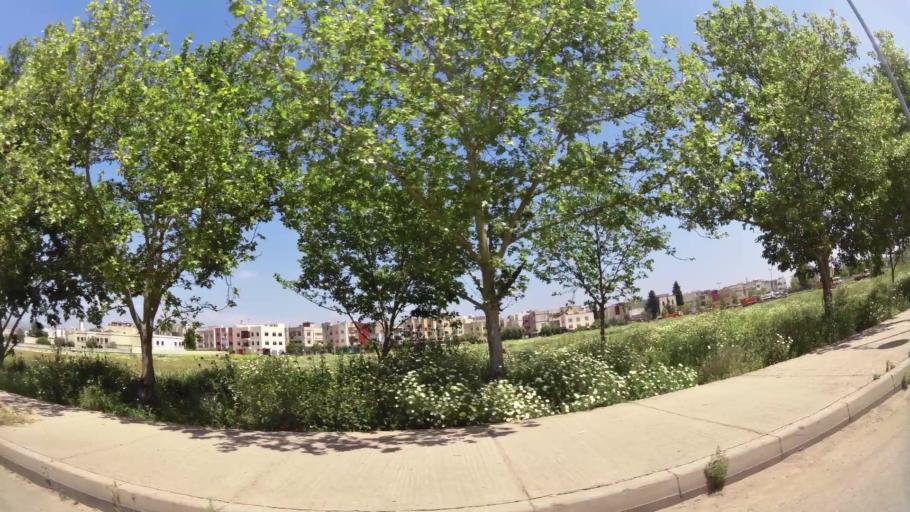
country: MA
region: Fes-Boulemane
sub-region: Fes
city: Fes
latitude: 34.0282
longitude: -5.0281
